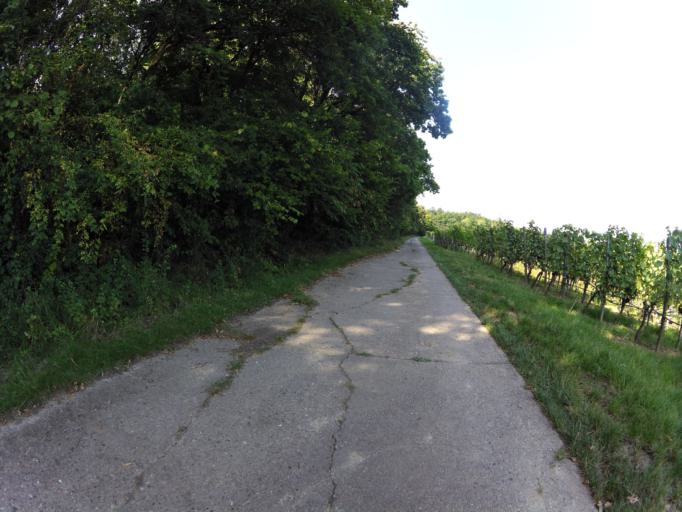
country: DE
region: Bavaria
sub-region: Regierungsbezirk Unterfranken
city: Nordheim
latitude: 49.8451
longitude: 10.1652
